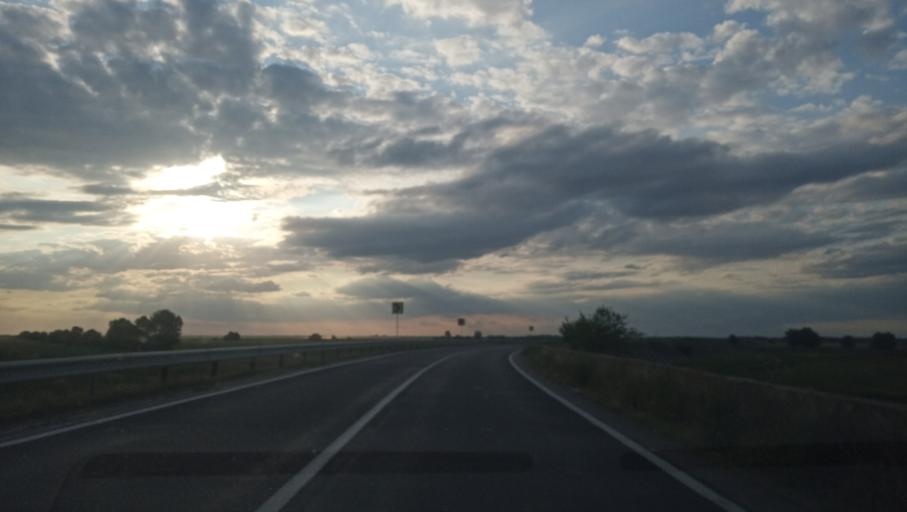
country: RO
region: Calarasi
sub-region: Municipiul Calarasi
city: Calarasi
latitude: 44.2023
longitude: 27.2875
